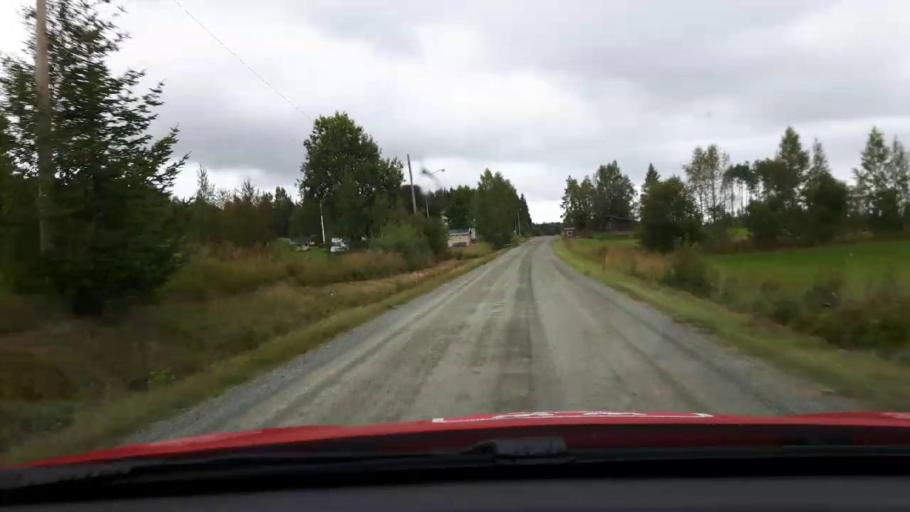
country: SE
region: Jaemtland
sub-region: Bergs Kommun
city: Hoverberg
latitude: 62.8673
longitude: 14.2987
